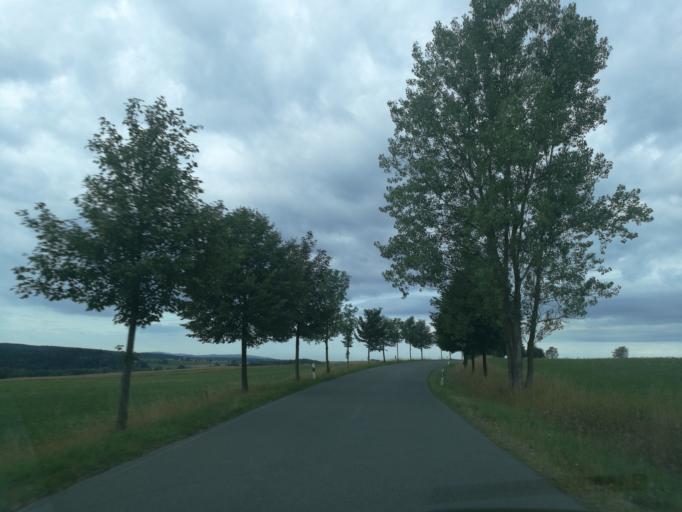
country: DE
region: Saxony
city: Triebel
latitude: 50.3287
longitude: 12.1066
